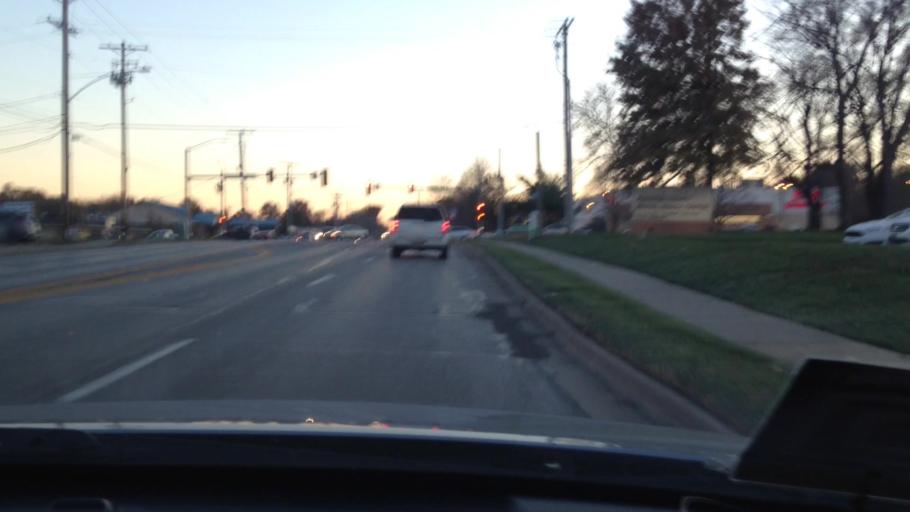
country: US
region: Kansas
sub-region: Johnson County
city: Merriam
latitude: 39.0116
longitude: -94.7145
